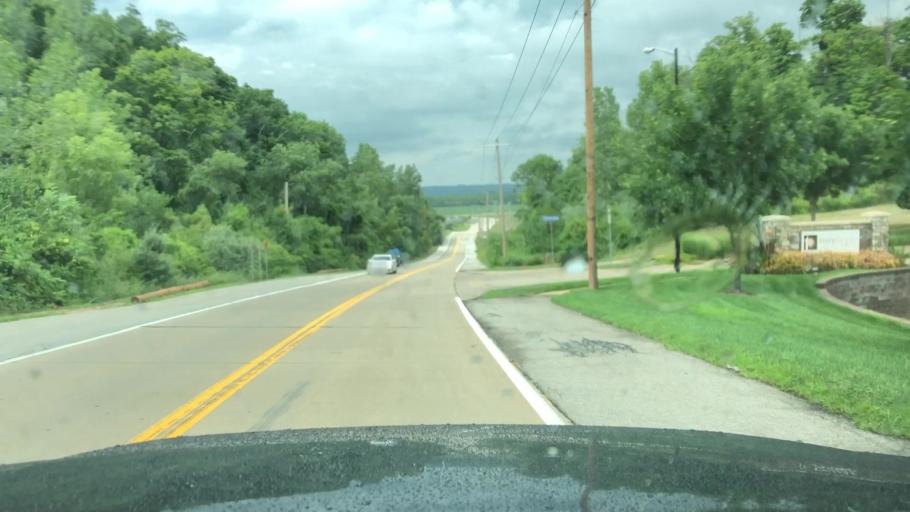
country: US
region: Missouri
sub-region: Saint Charles County
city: Saint Peters
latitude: 38.8008
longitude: -90.5807
